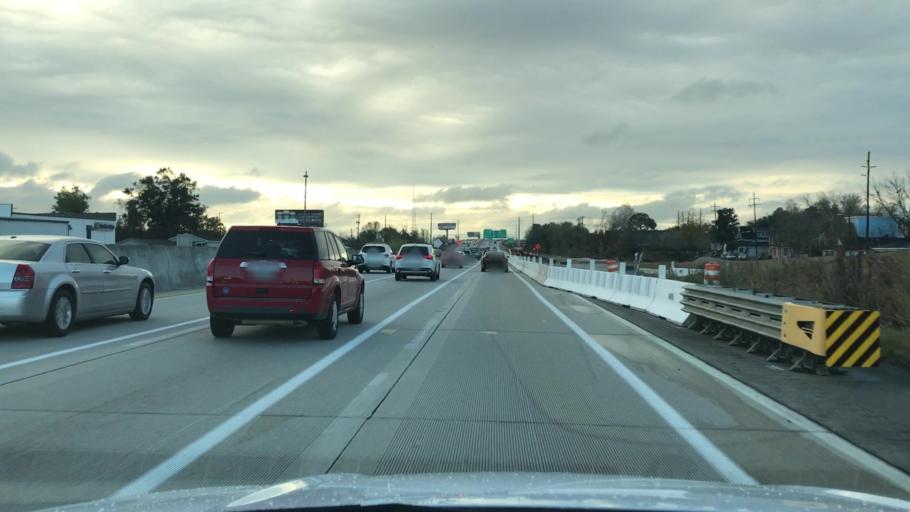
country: US
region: South Carolina
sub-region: Charleston County
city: North Charleston
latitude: 32.8320
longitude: -79.9568
